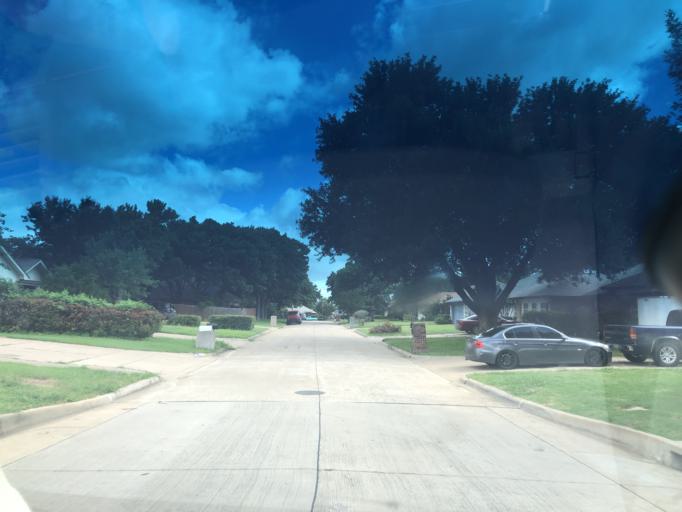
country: US
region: Texas
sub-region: Dallas County
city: Grand Prairie
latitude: 32.7061
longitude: -97.0333
